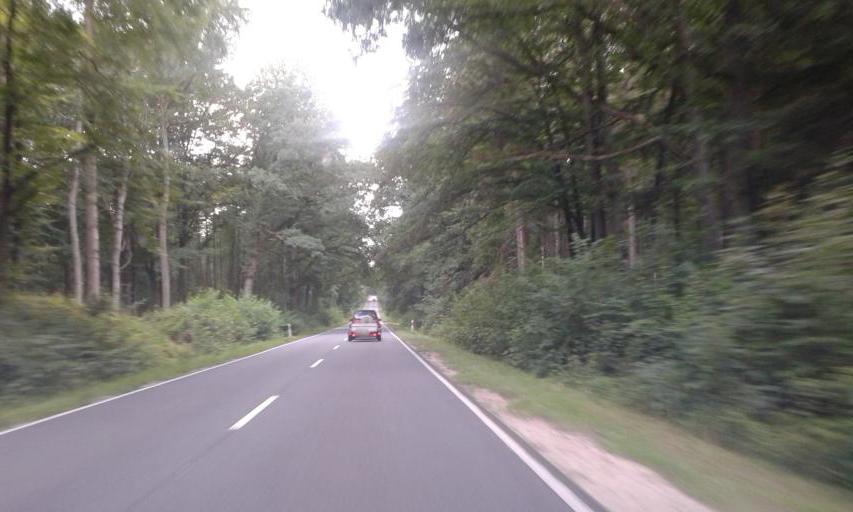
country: PL
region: West Pomeranian Voivodeship
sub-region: Powiat szczecinecki
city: Grzmiaca
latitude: 53.7197
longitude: 16.4929
